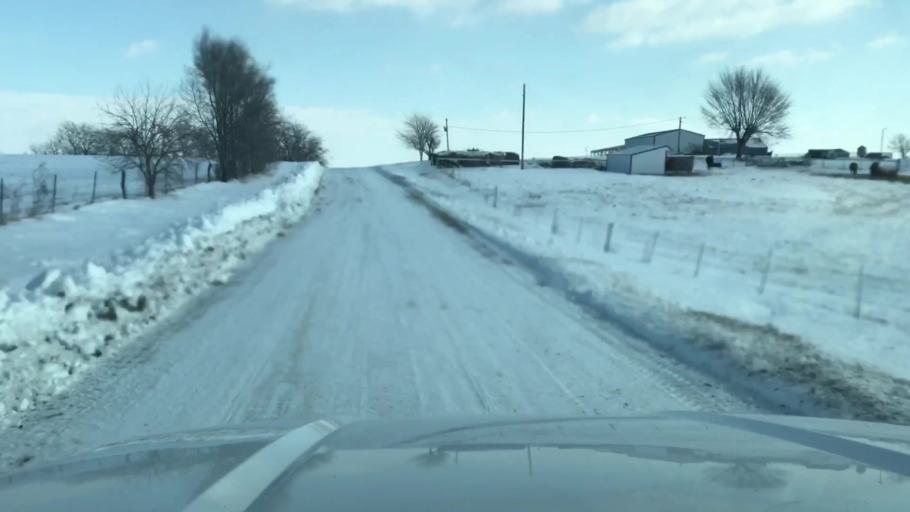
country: US
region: Missouri
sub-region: Nodaway County
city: Maryville
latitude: 40.3868
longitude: -94.7118
